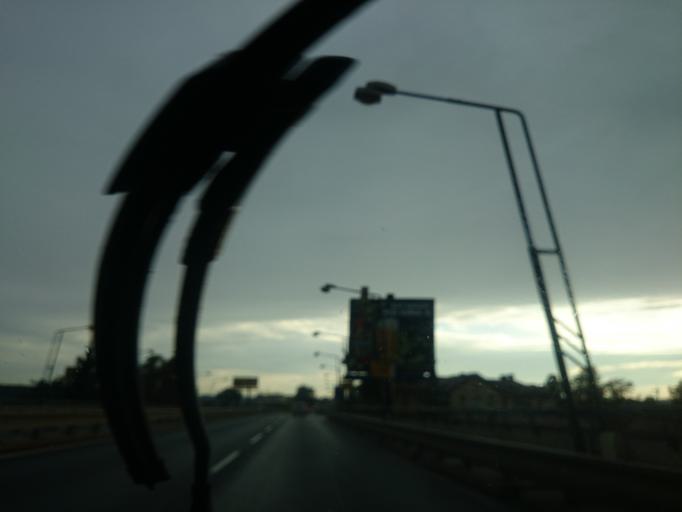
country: CZ
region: Olomoucky
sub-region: Okres Olomouc
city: Olomouc
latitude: 49.5851
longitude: 17.2725
